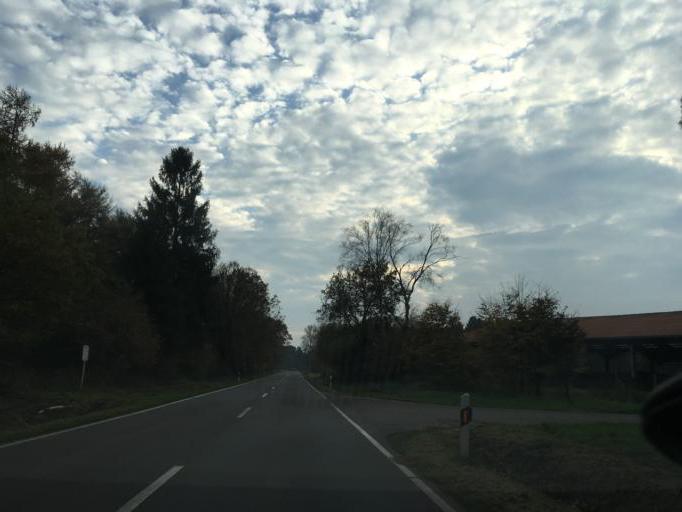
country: DE
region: Lower Saxony
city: Bispingen
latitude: 53.0119
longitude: 9.9983
